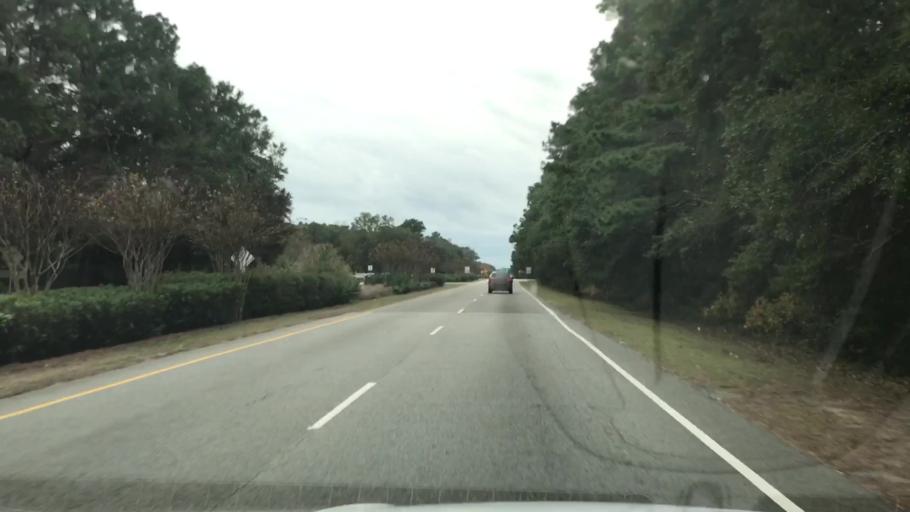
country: US
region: South Carolina
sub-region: Georgetown County
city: Murrells Inlet
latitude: 33.4951
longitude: -79.0873
